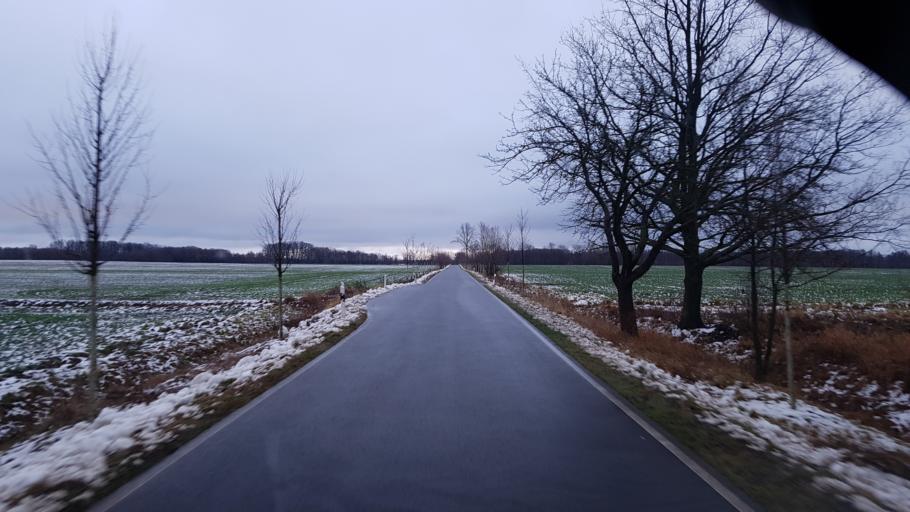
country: DE
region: Brandenburg
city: Luckau
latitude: 51.8064
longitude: 13.7201
